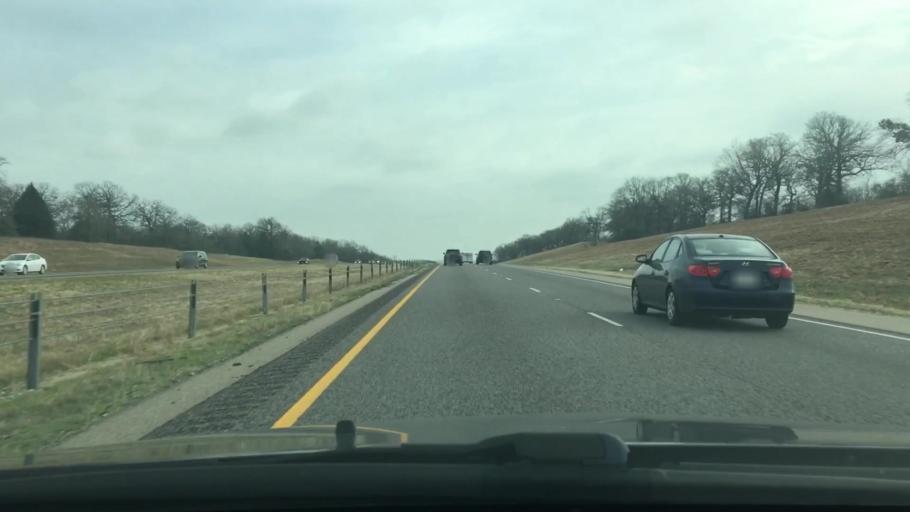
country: US
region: Texas
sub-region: Leon County
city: Buffalo
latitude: 31.5324
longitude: -96.1178
